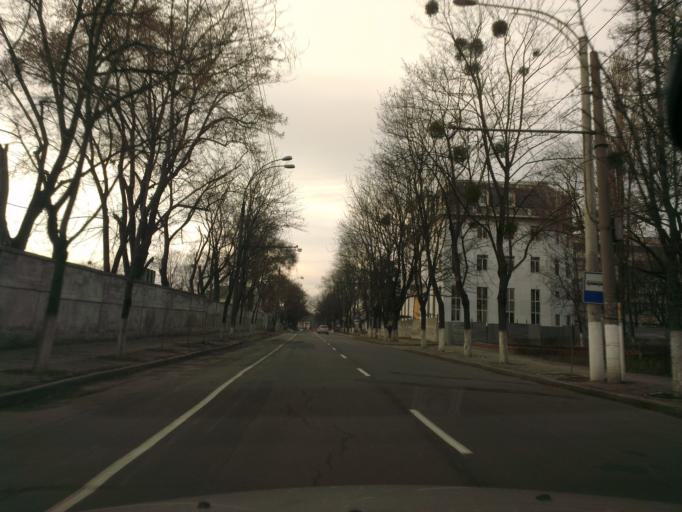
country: MD
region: Chisinau
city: Chisinau
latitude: 47.0268
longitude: 28.8203
